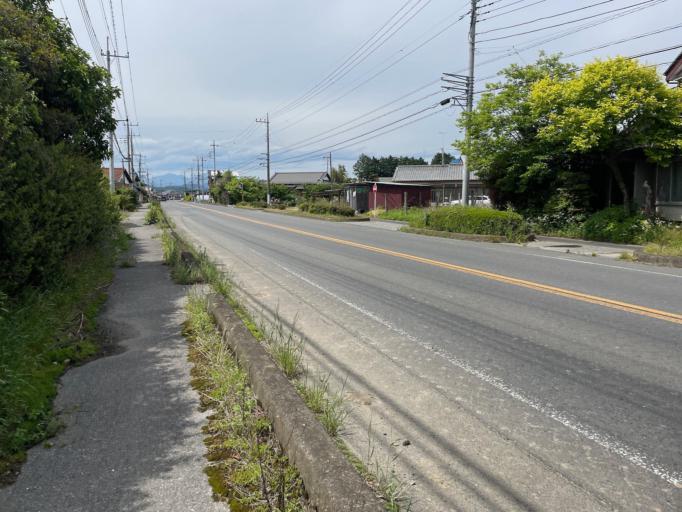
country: JP
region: Tochigi
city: Mibu
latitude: 36.4662
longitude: 139.7669
